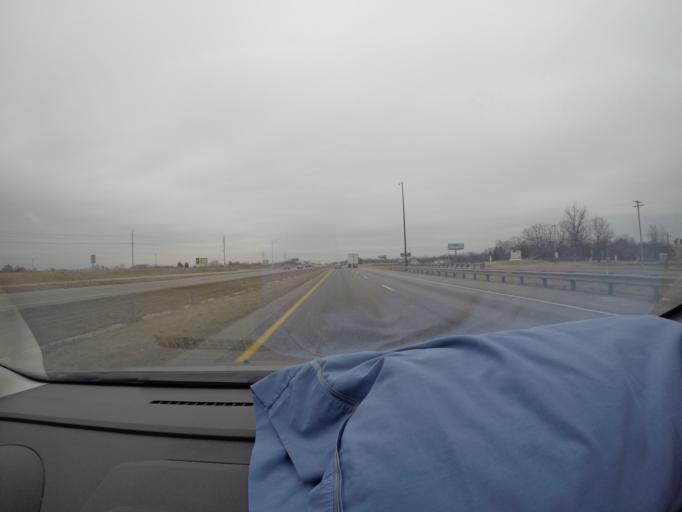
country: US
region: Missouri
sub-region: Saint Charles County
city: Wentzville
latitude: 38.8106
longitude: -90.9311
